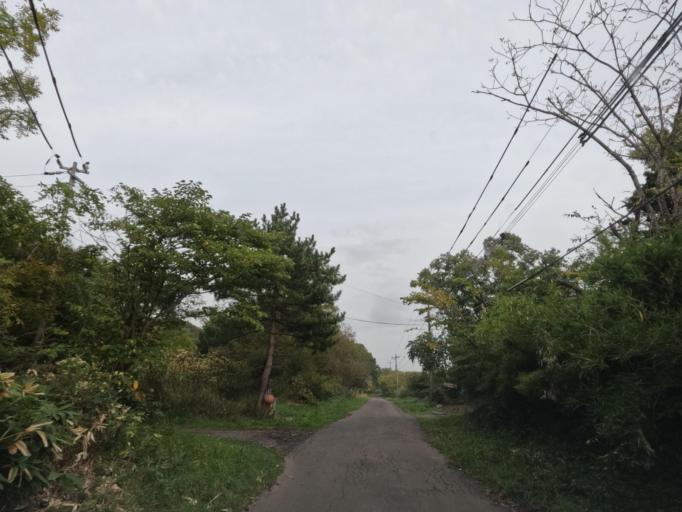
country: JP
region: Hokkaido
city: Date
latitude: 42.4124
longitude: 140.9232
